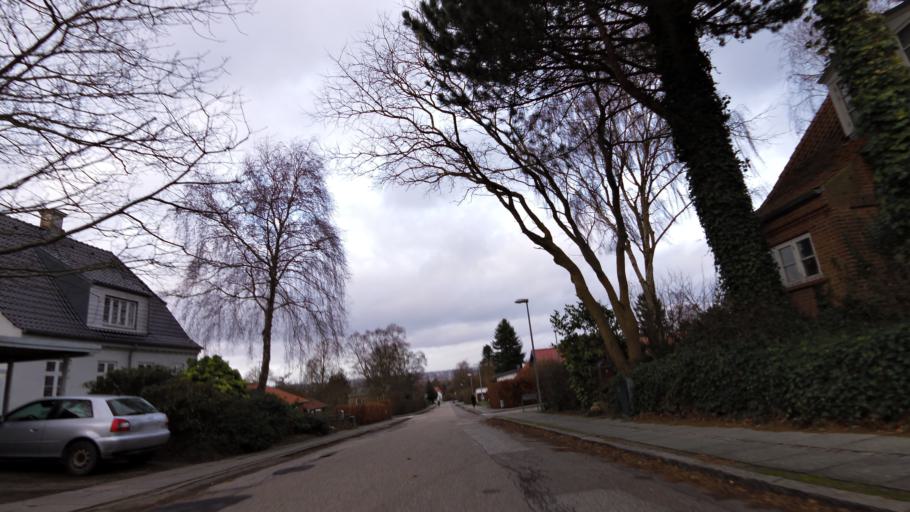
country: DK
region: Central Jutland
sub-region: Arhus Kommune
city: Arhus
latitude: 56.1281
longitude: 10.1889
